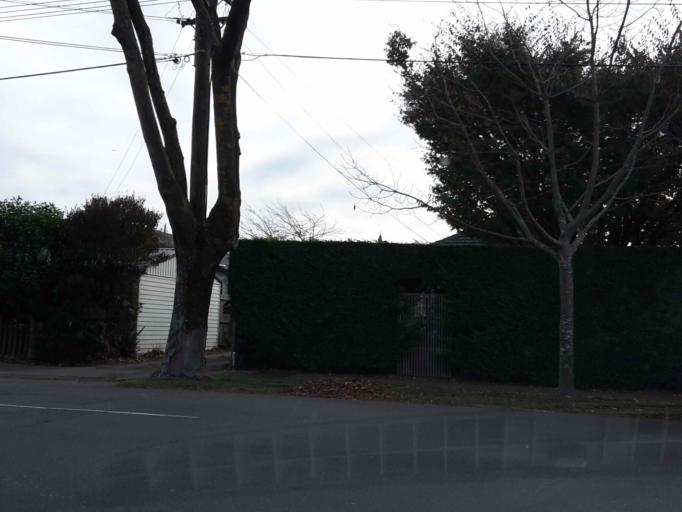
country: NZ
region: Canterbury
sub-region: Christchurch City
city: Christchurch
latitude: -43.5664
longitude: 172.6200
